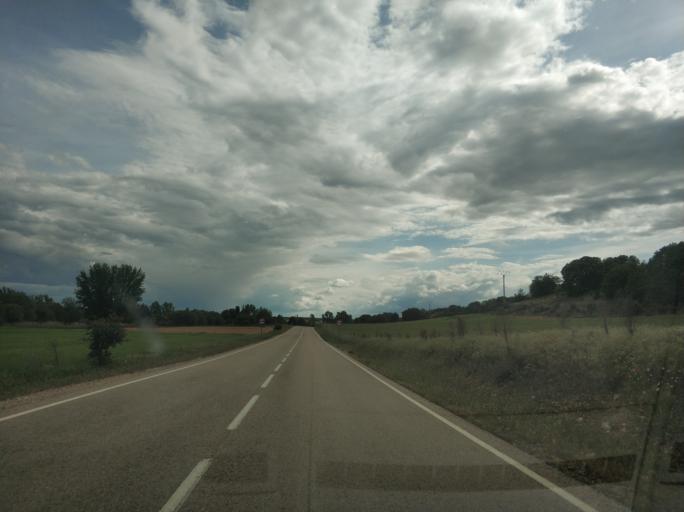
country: ES
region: Castille and Leon
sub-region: Provincia de Soria
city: Alcubilla de Avellaneda
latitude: 41.7393
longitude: -3.2934
